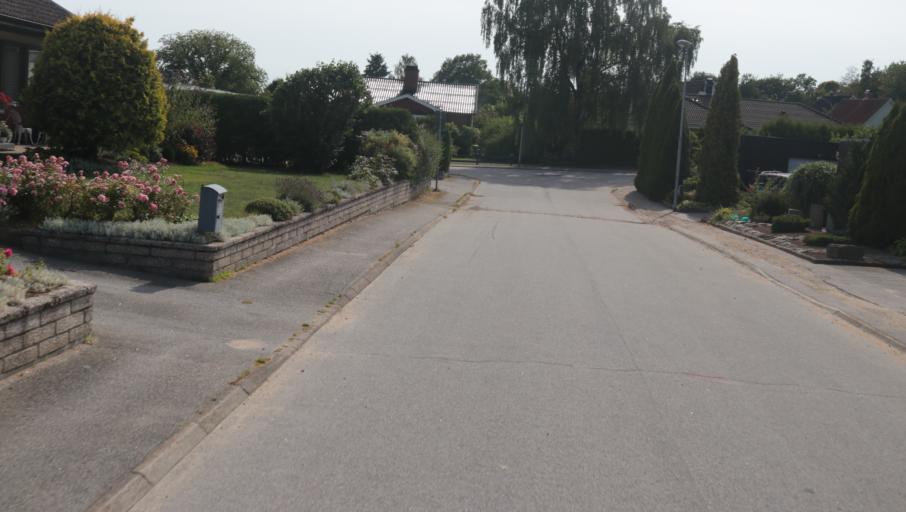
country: SE
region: Blekinge
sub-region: Karlshamns Kommun
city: Karlshamn
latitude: 56.2085
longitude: 14.8415
